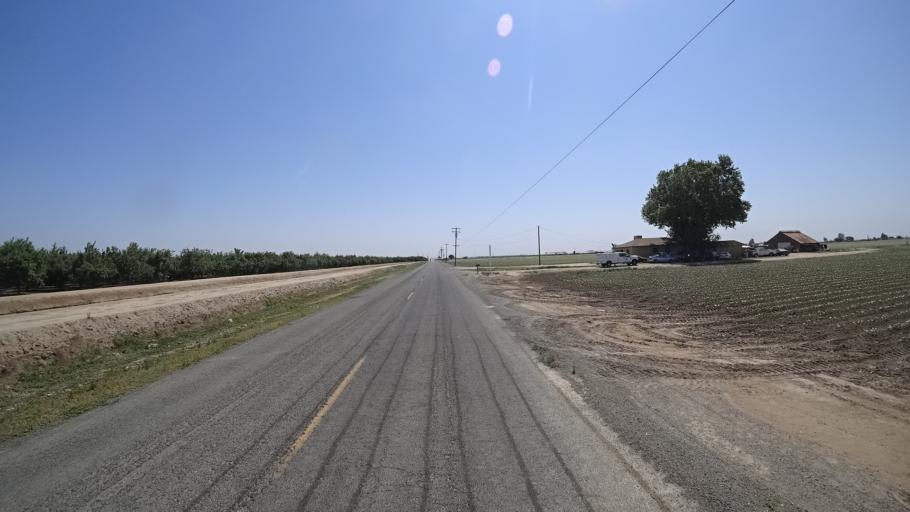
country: US
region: California
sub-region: Kings County
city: Home Garden
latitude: 36.2840
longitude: -119.6259
